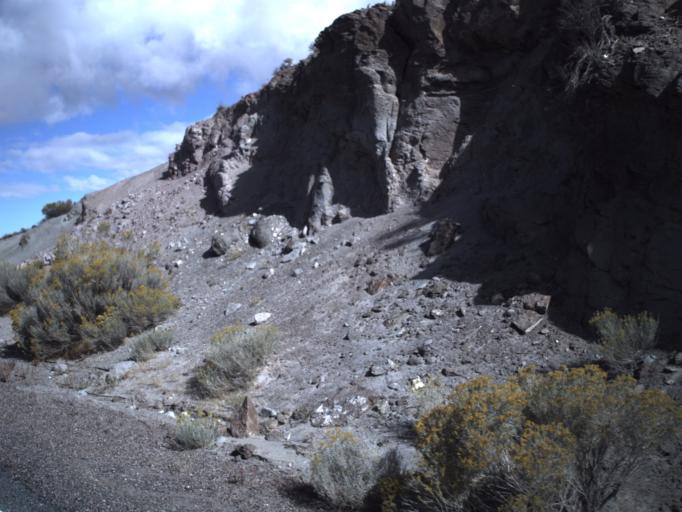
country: US
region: Utah
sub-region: Beaver County
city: Milford
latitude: 38.6162
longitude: -113.8431
